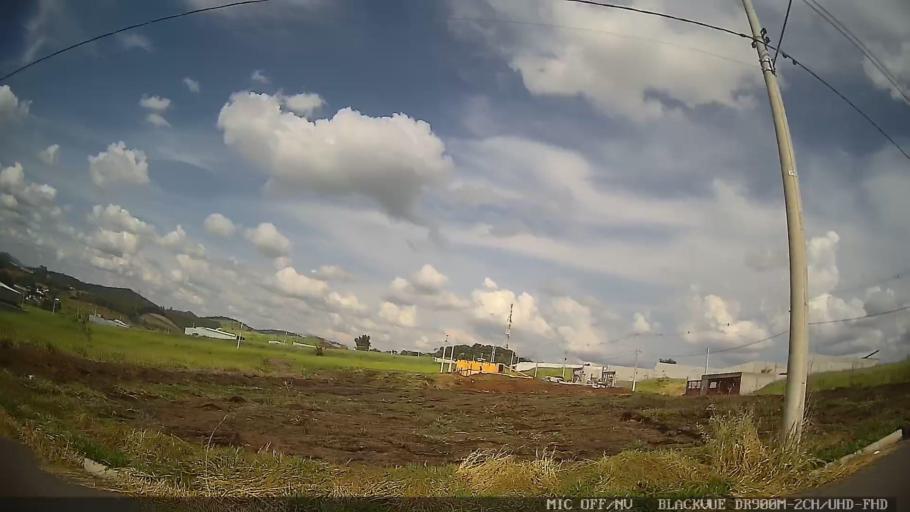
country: BR
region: Sao Paulo
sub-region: Atibaia
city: Atibaia
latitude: -23.0740
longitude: -46.5753
